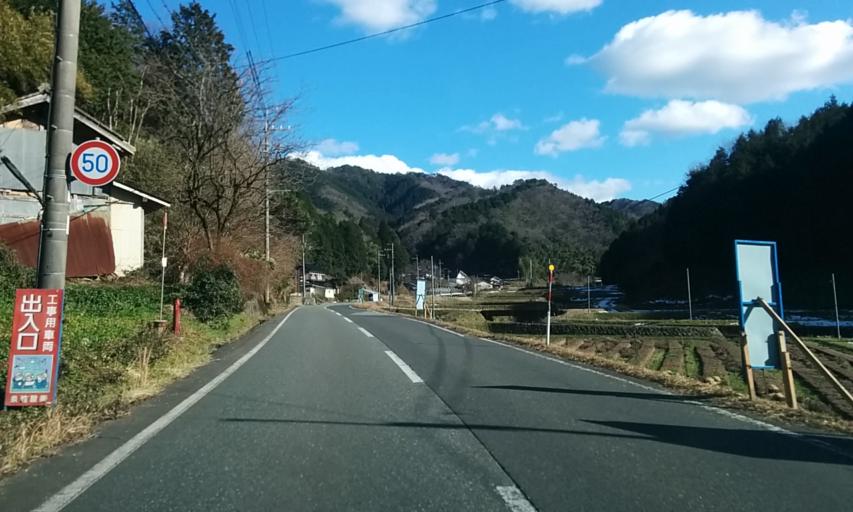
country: JP
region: Hyogo
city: Toyooka
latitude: 35.4317
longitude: 134.9541
